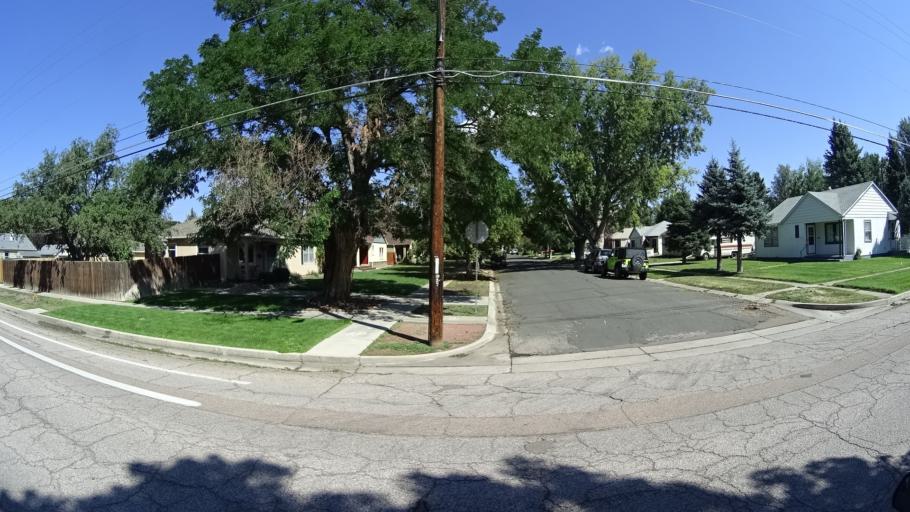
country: US
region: Colorado
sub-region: El Paso County
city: Colorado Springs
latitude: 38.8651
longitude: -104.8116
